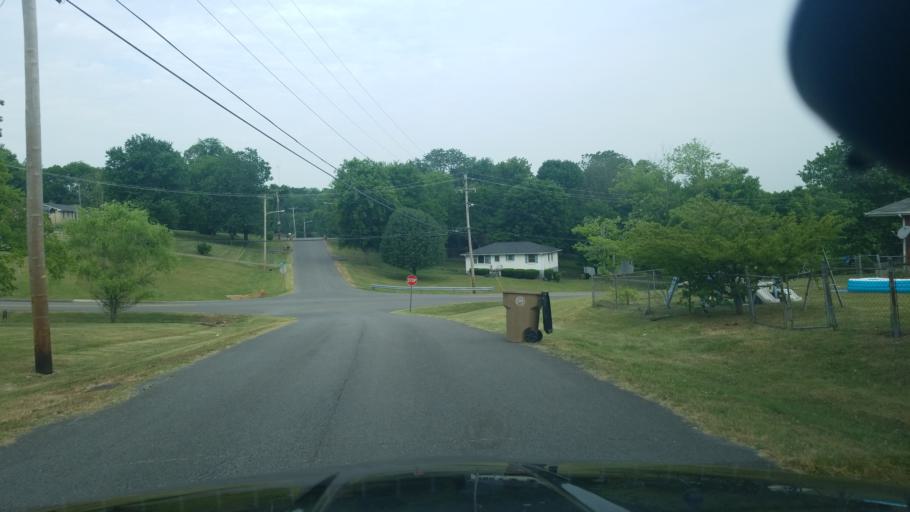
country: US
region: Tennessee
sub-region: Davidson County
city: Goodlettsville
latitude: 36.2623
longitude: -86.7419
